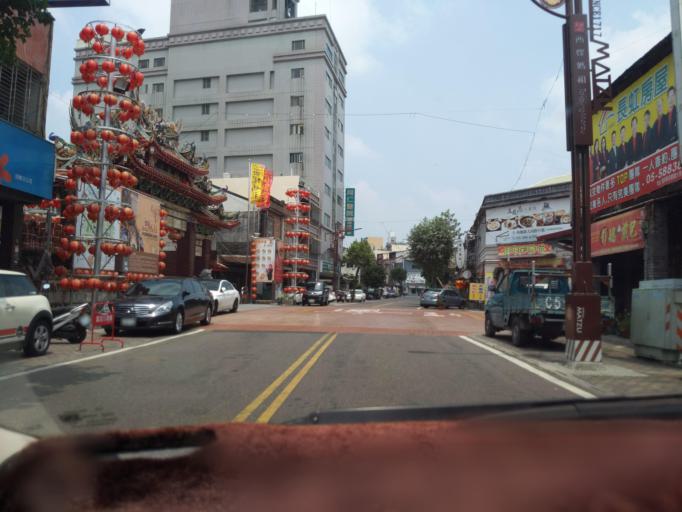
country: TW
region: Taiwan
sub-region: Yunlin
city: Douliu
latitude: 23.8012
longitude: 120.4603
